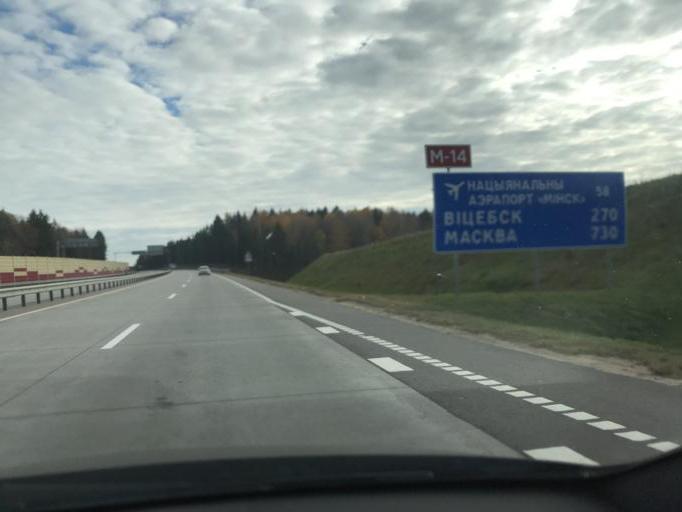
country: BY
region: Minsk
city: Zaslawye
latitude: 54.0672
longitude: 27.2945
